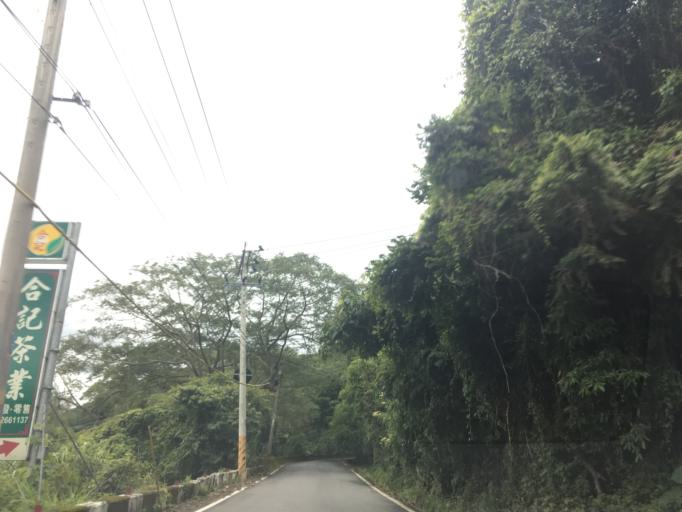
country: TW
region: Taiwan
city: Lugu
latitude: 23.5305
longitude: 120.7055
